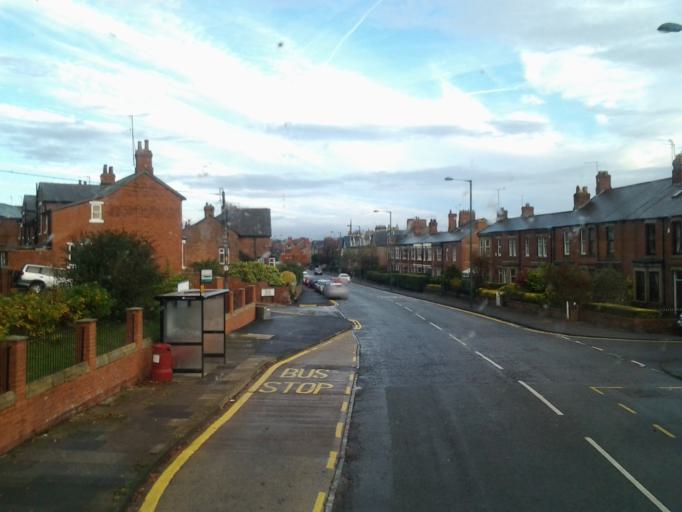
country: GB
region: England
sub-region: County Durham
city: Chester-le-Street
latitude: 54.8491
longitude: -1.5732
